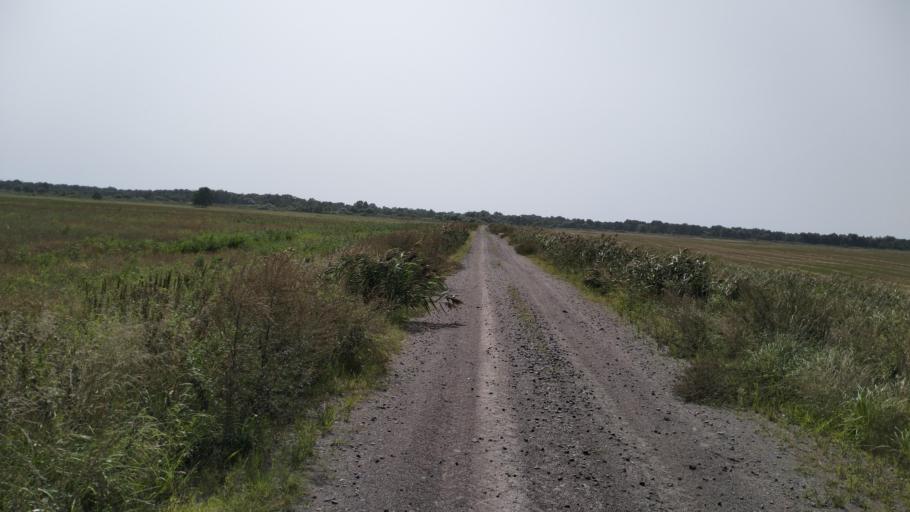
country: BY
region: Brest
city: Davyd-Haradok
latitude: 51.9744
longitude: 27.1742
